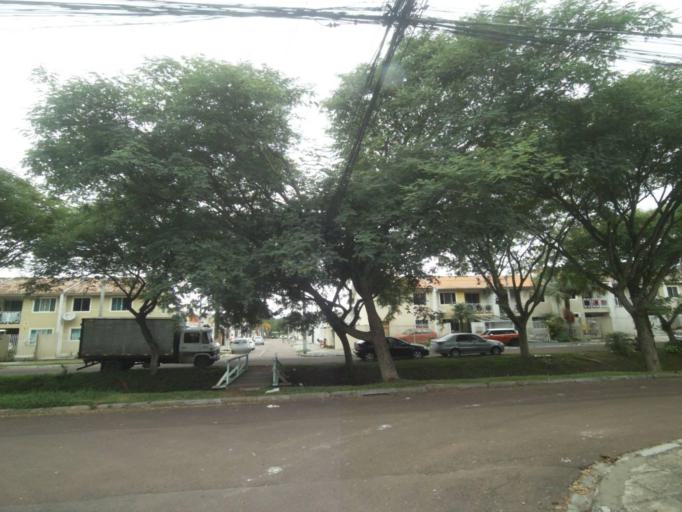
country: BR
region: Parana
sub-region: Araucaria
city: Araucaria
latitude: -25.5499
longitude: -49.3429
